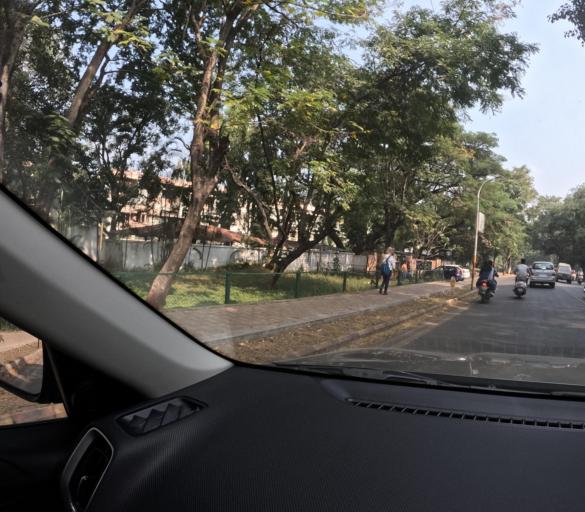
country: IN
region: Maharashtra
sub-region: Pune Division
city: Pune
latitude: 18.5235
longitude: 73.8844
